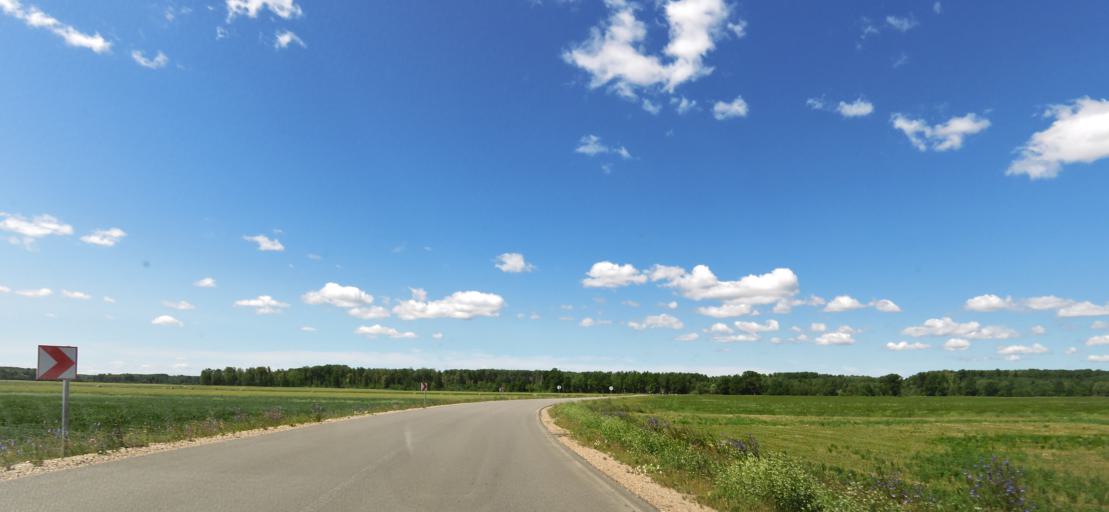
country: LT
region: Panevezys
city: Pasvalys
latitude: 56.2248
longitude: 24.4956
